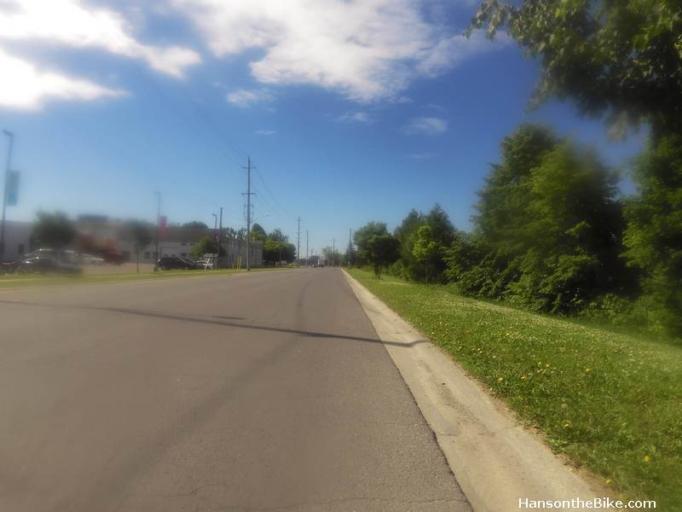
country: CA
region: Ontario
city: Kingston
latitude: 44.2228
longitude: -76.5306
